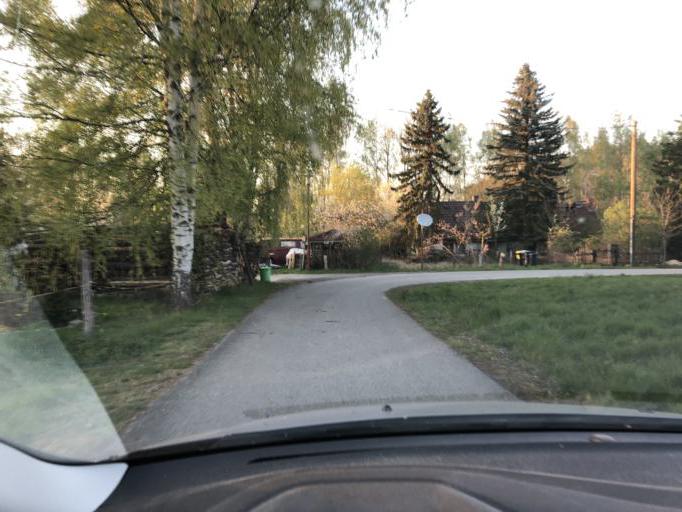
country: DE
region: Saxony
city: Gross Duben
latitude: 51.5756
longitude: 14.5531
